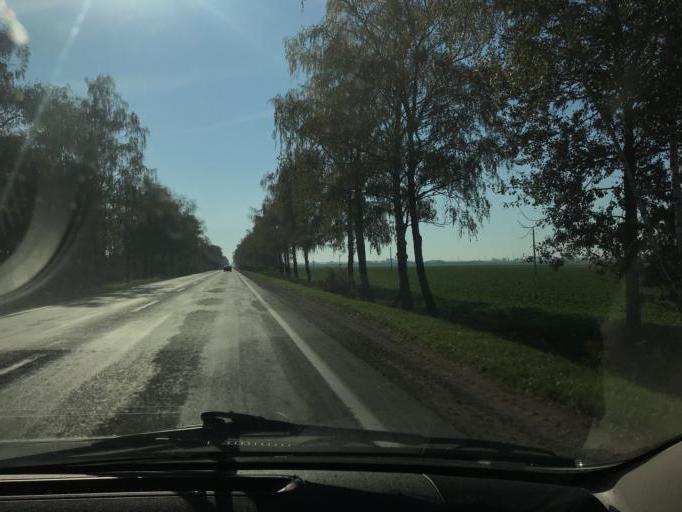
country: BY
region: Minsk
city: Salihorsk
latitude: 52.8228
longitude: 27.4655
